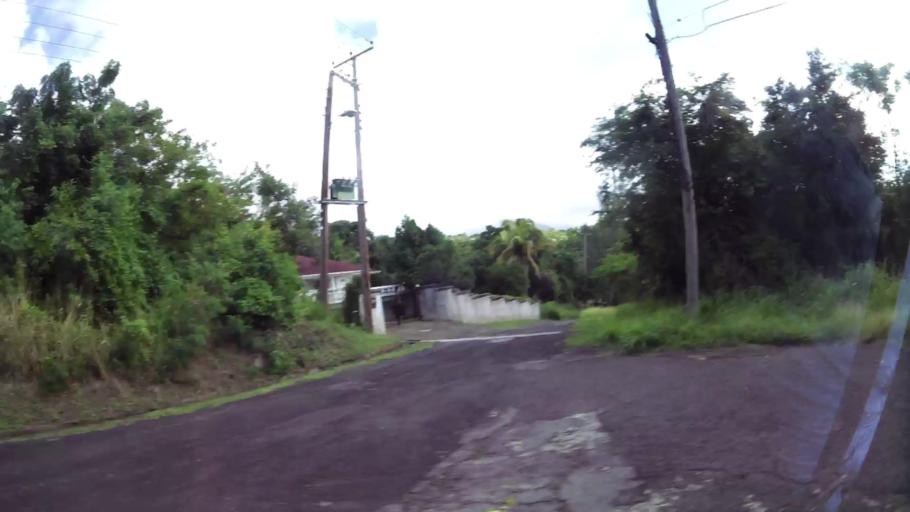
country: MS
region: Saint Peter
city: Saint Peters
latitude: 16.7532
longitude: -62.2232
